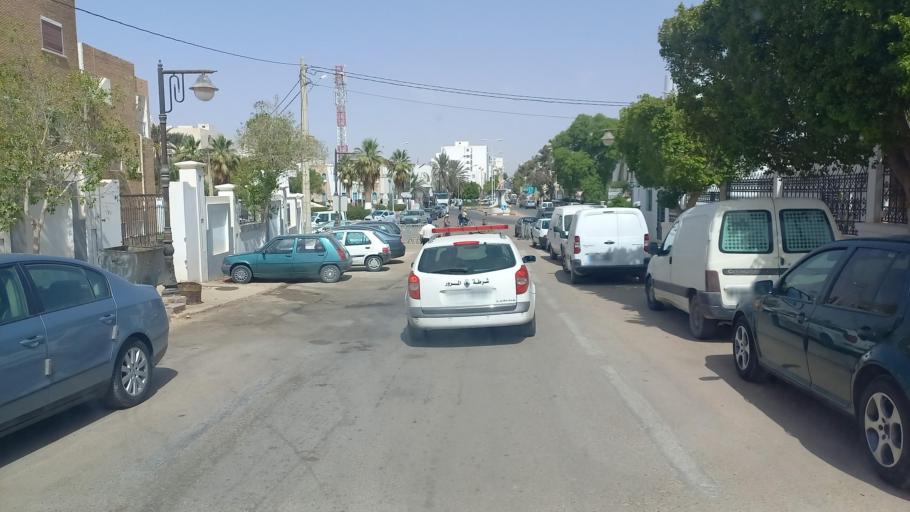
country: TN
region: Madanin
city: Medenine
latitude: 33.3425
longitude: 10.4919
